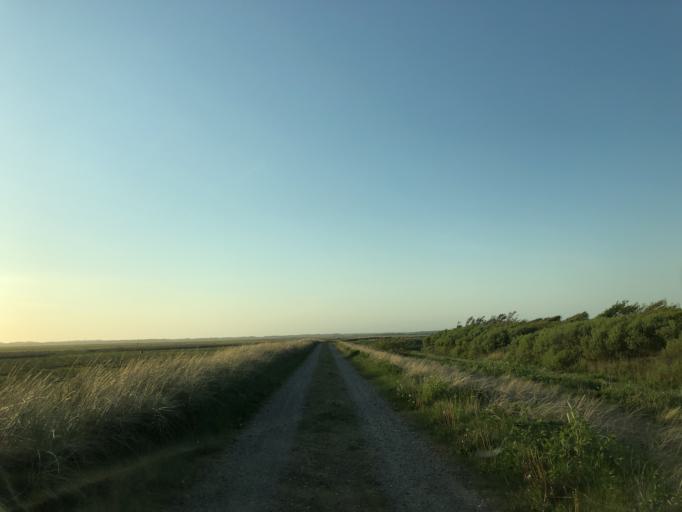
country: DK
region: Central Jutland
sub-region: Holstebro Kommune
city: Ulfborg
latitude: 56.2298
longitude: 8.1664
